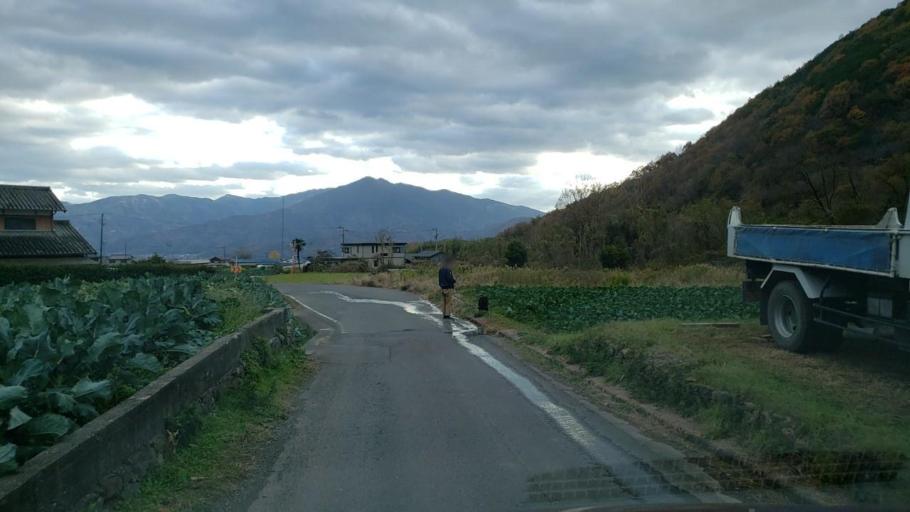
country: JP
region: Tokushima
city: Wakimachi
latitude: 34.1070
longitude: 134.2241
